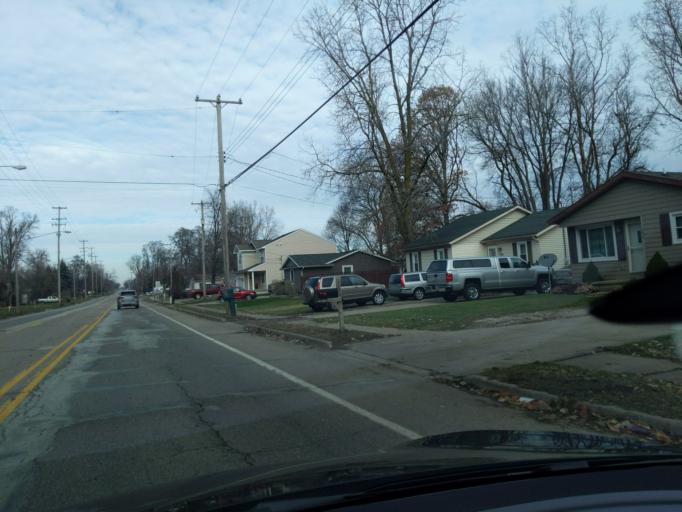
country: US
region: Michigan
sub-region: Ingham County
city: Holt
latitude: 42.6551
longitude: -84.5235
